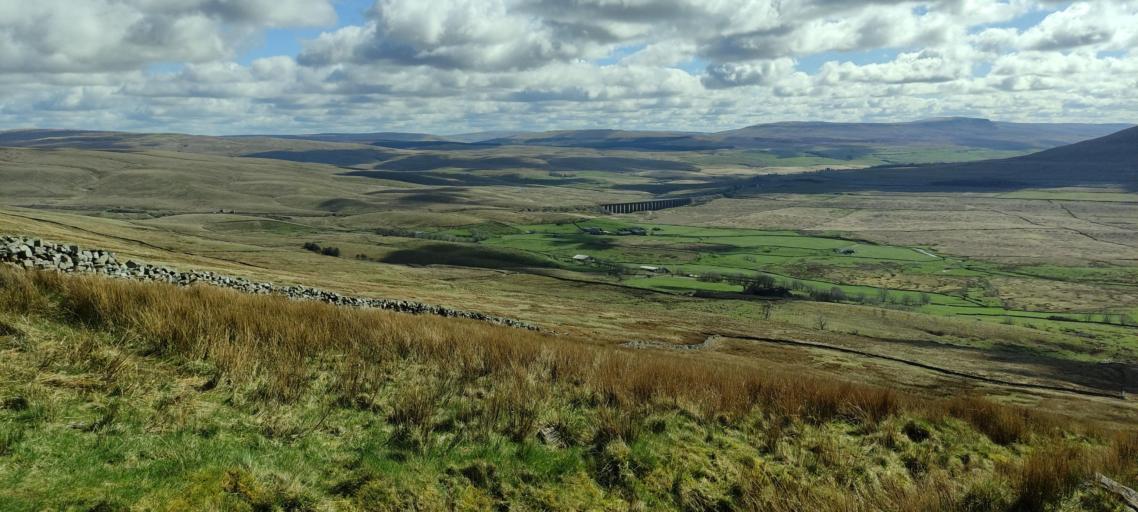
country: GB
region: England
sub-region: North Yorkshire
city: Ingleton
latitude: 54.2156
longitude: -2.4074
